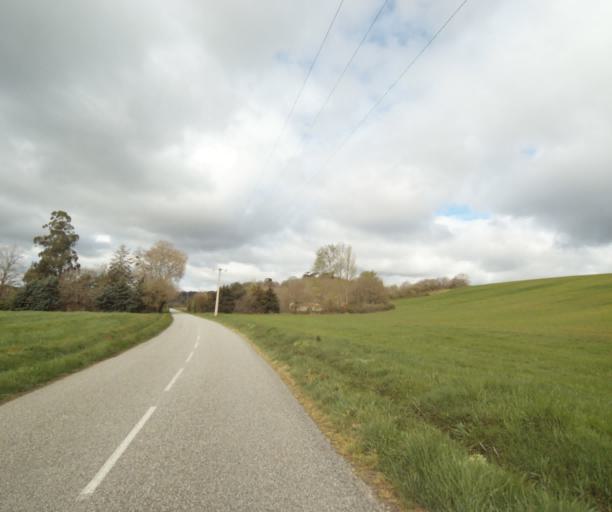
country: FR
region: Midi-Pyrenees
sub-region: Departement de l'Ariege
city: Saverdun
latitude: 43.2274
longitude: 1.5544
